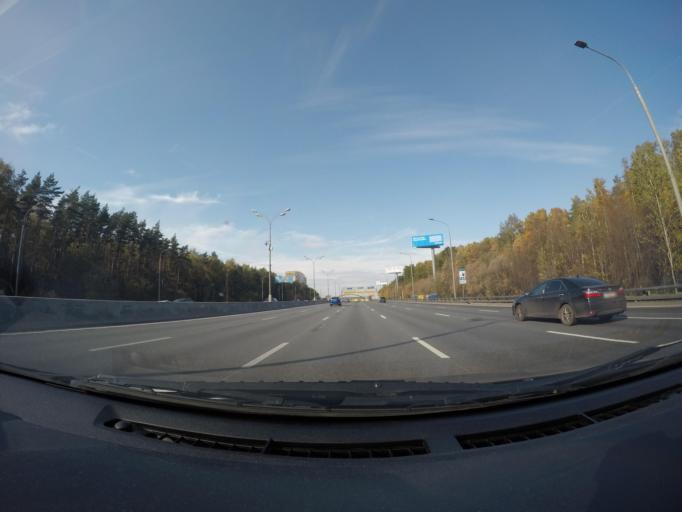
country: RU
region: Moskovskaya
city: Druzhba
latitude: 55.8755
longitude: 37.7397
